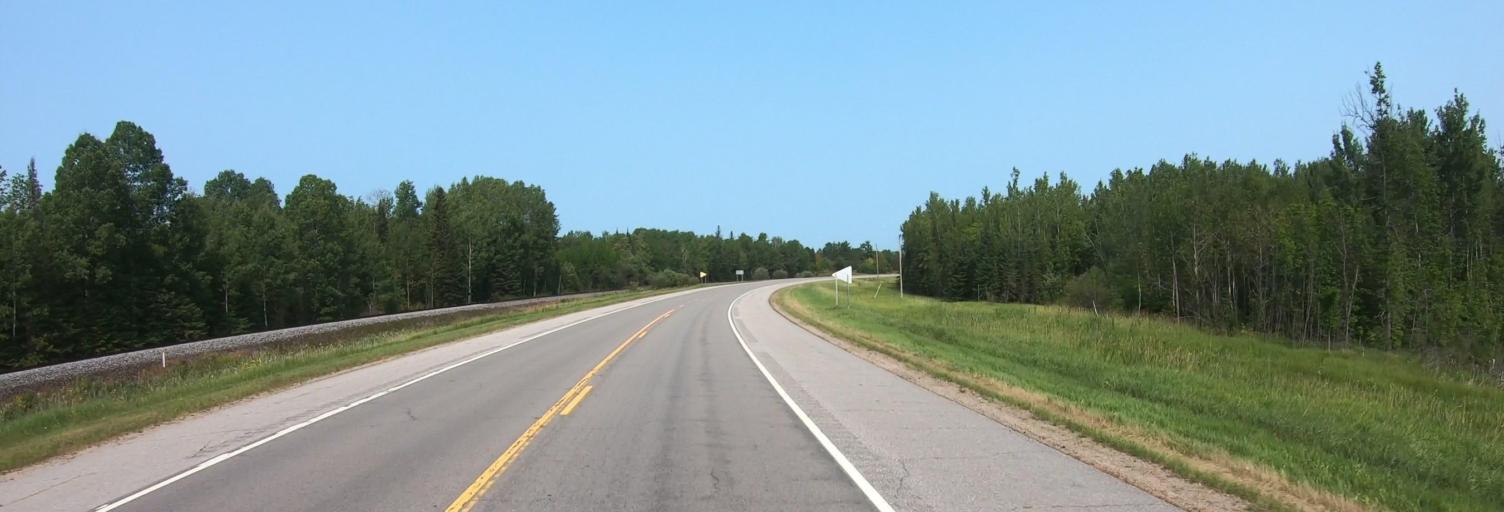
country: US
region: Minnesota
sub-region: Saint Louis County
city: Mountain Iron
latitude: 48.0951
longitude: -92.8419
